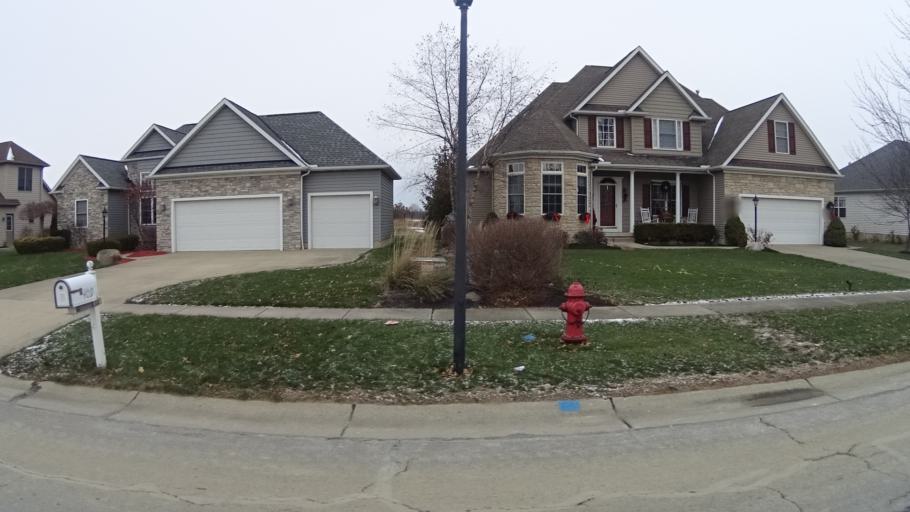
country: US
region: Ohio
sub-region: Lorain County
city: Lagrange
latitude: 41.2487
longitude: -82.1096
